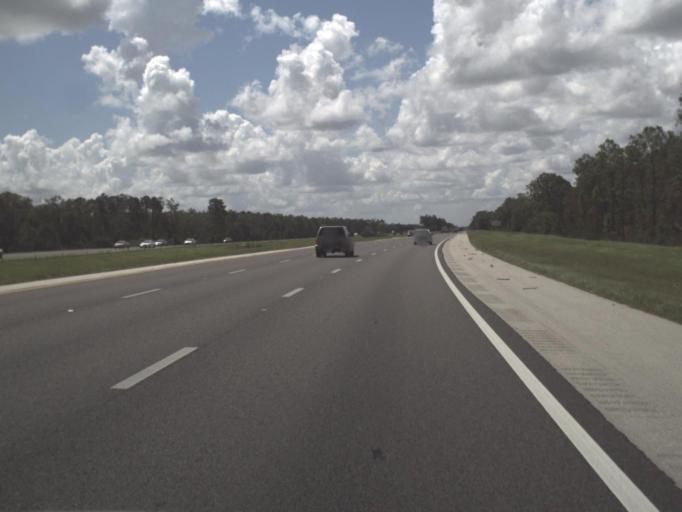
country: US
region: Florida
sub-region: Lee County
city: Estero
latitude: 26.4193
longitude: -81.7738
